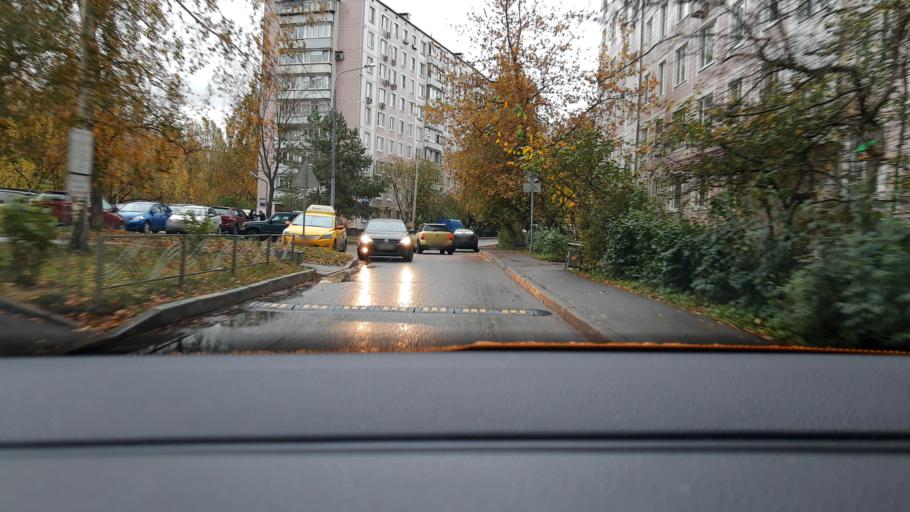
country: RU
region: Moscow
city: Strogino
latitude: 55.8136
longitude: 37.4016
